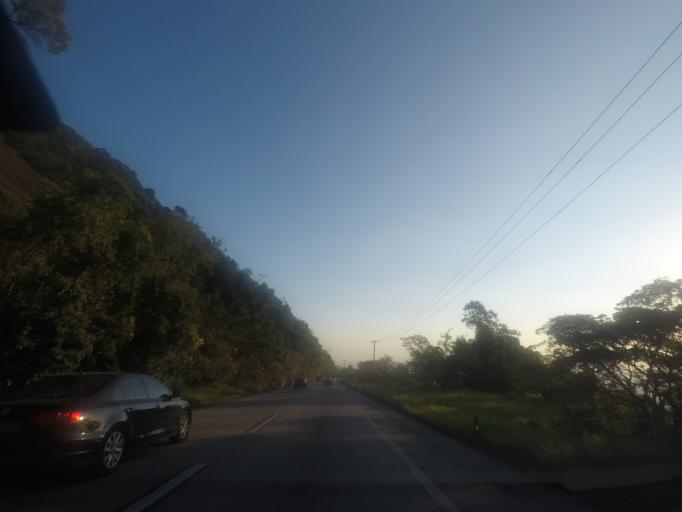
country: BR
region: Rio de Janeiro
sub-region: Petropolis
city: Petropolis
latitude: -22.5269
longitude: -43.2345
